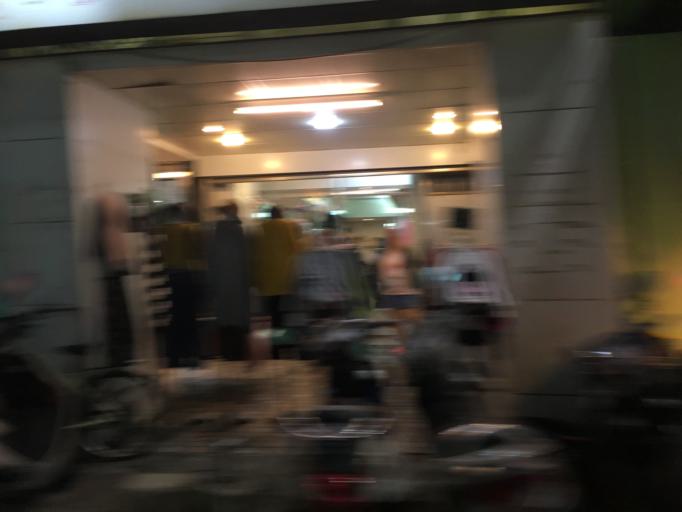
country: TW
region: Taiwan
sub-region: Hsinchu
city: Hsinchu
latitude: 24.8043
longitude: 120.9672
